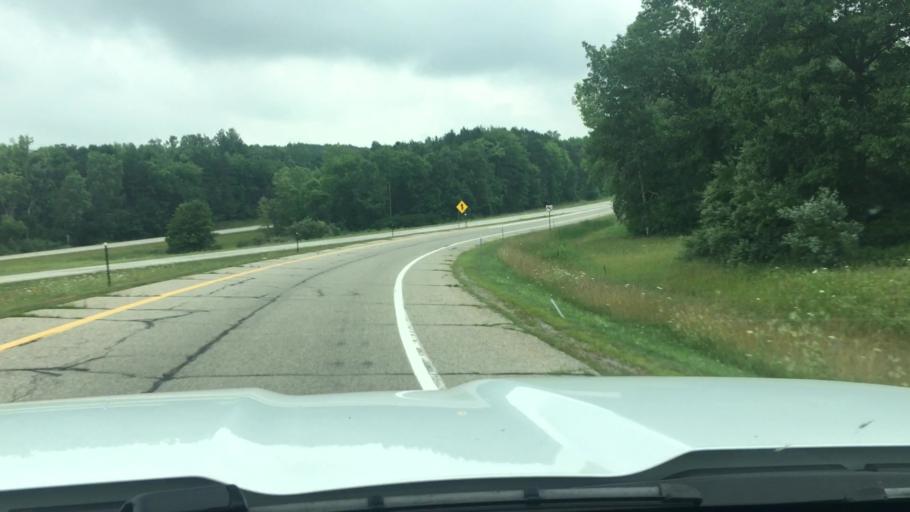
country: US
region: Michigan
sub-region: Lapeer County
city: Lapeer
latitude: 43.0064
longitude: -83.2144
